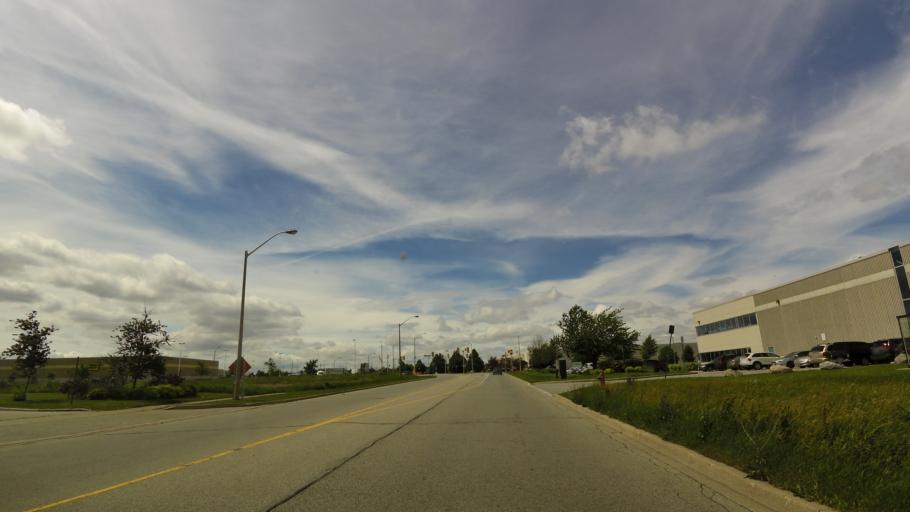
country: CA
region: Ontario
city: Oakville
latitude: 43.5161
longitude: -79.6831
